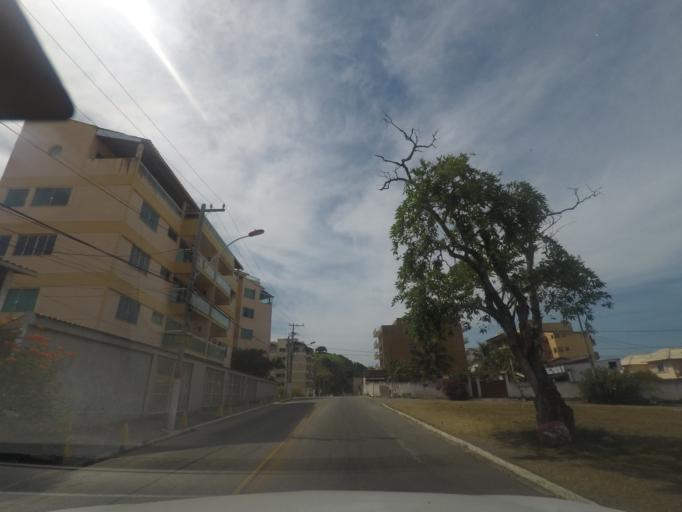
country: BR
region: Rio de Janeiro
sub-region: Marica
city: Marica
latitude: -22.9556
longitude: -42.6954
